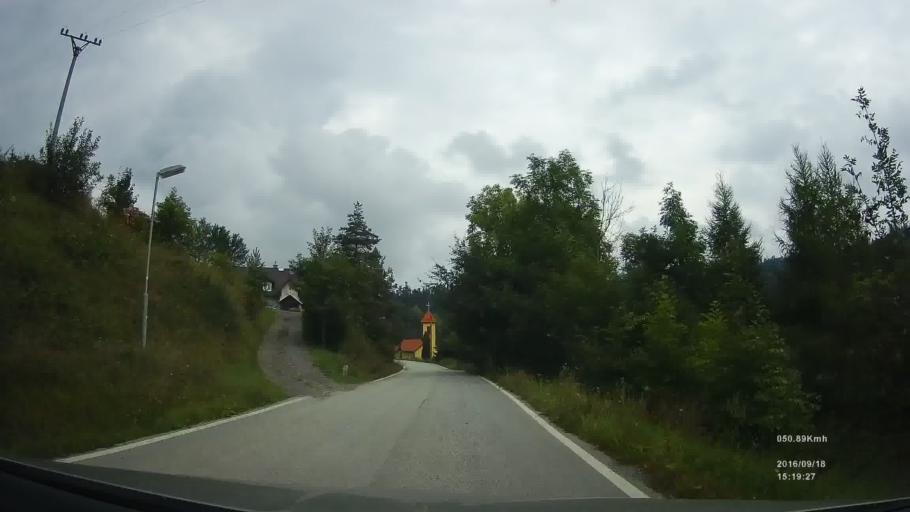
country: SK
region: Presovsky
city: Lubica
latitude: 49.0383
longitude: 20.4901
